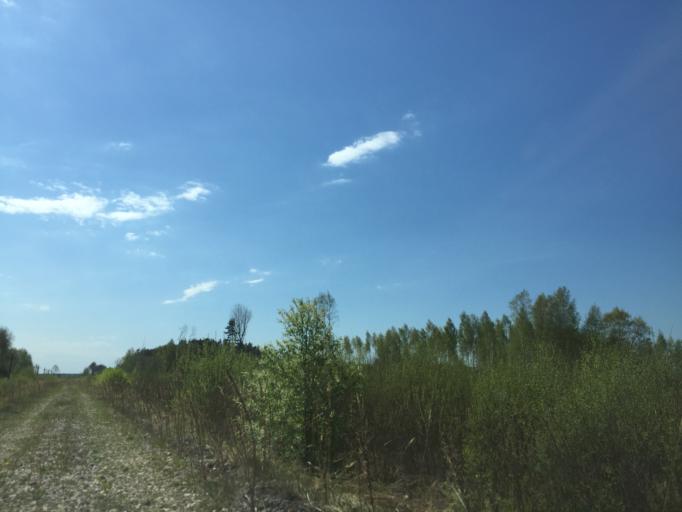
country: LV
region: Saulkrastu
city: Saulkrasti
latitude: 57.3455
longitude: 24.4837
